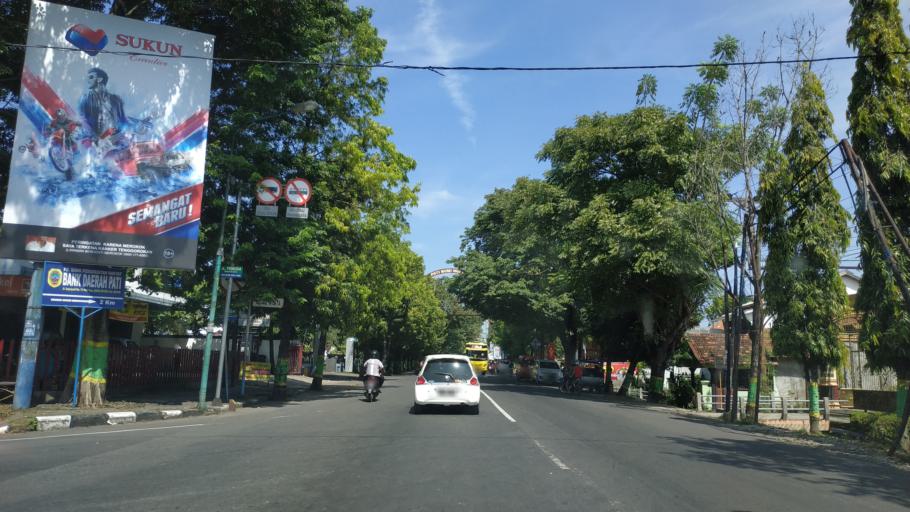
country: ID
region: Central Java
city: Baran
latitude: -6.7522
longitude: 111.0523
